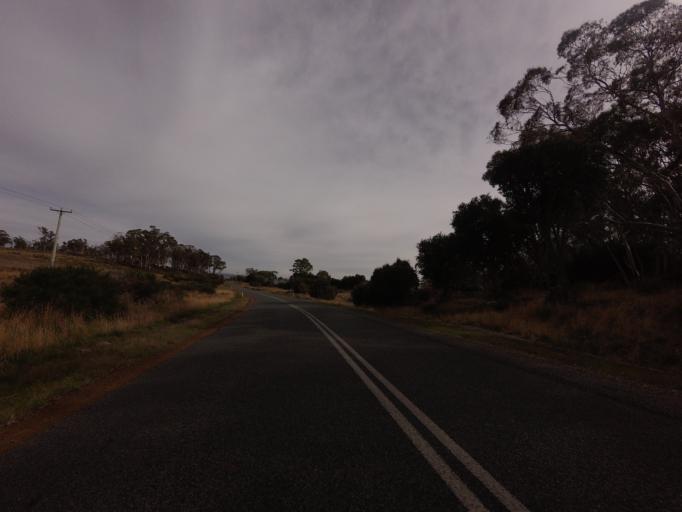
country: AU
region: Tasmania
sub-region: Brighton
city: Bridgewater
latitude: -42.3297
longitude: 147.3951
